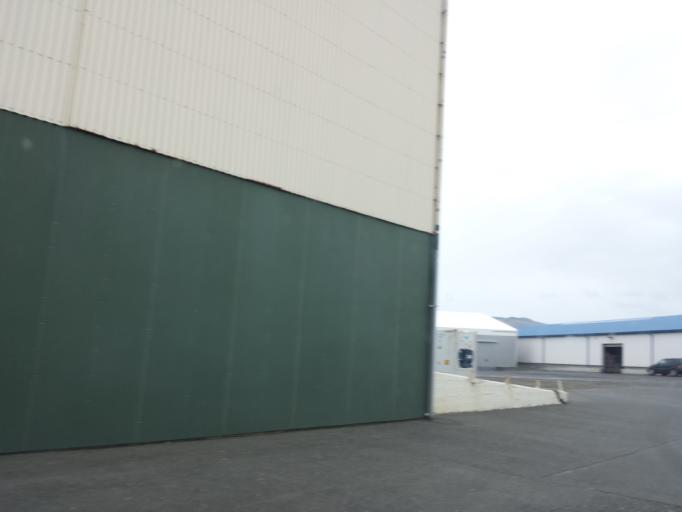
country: IS
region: West
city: Olafsvik
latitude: 64.9260
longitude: -23.2555
